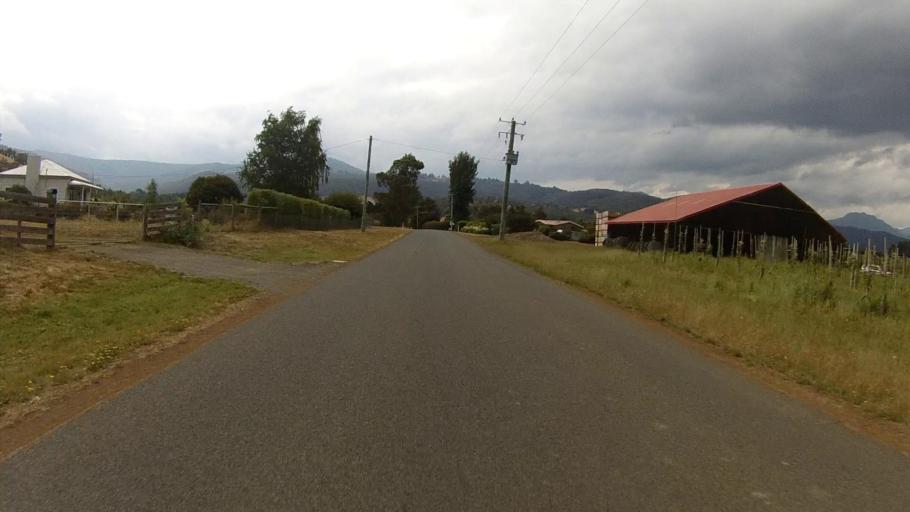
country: AU
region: Tasmania
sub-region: Huon Valley
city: Huonville
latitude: -42.9888
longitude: 147.0612
